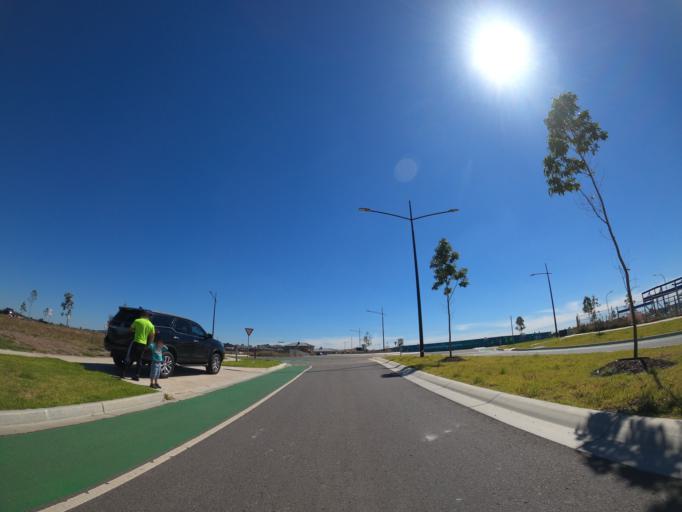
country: AU
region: Victoria
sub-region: Hume
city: Craigieburn
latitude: -37.5293
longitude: 144.9071
